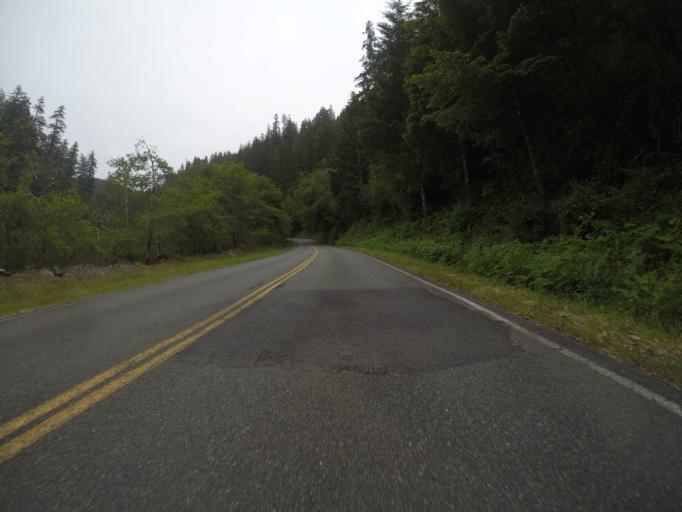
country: US
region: California
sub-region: Del Norte County
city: Bertsch-Oceanview
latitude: 41.7824
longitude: -124.0224
